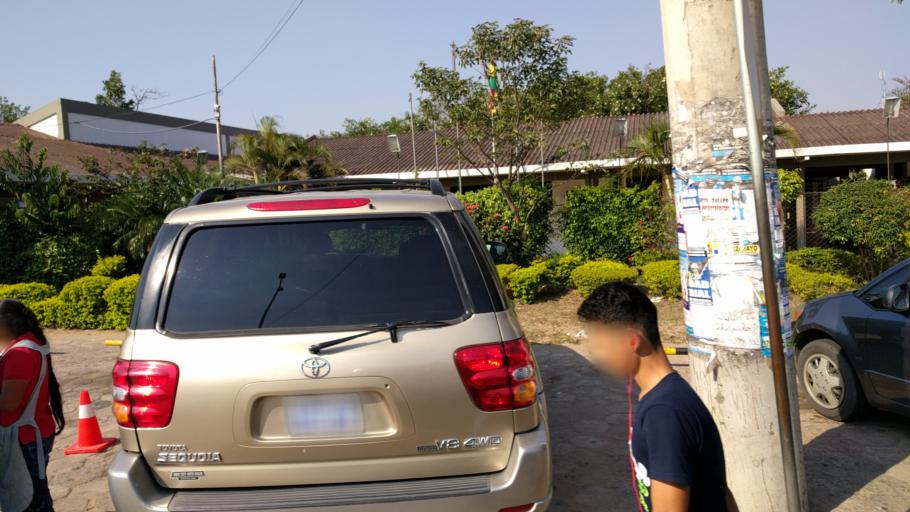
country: BO
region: Santa Cruz
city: Santa Cruz de la Sierra
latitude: -17.7791
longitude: -63.1547
